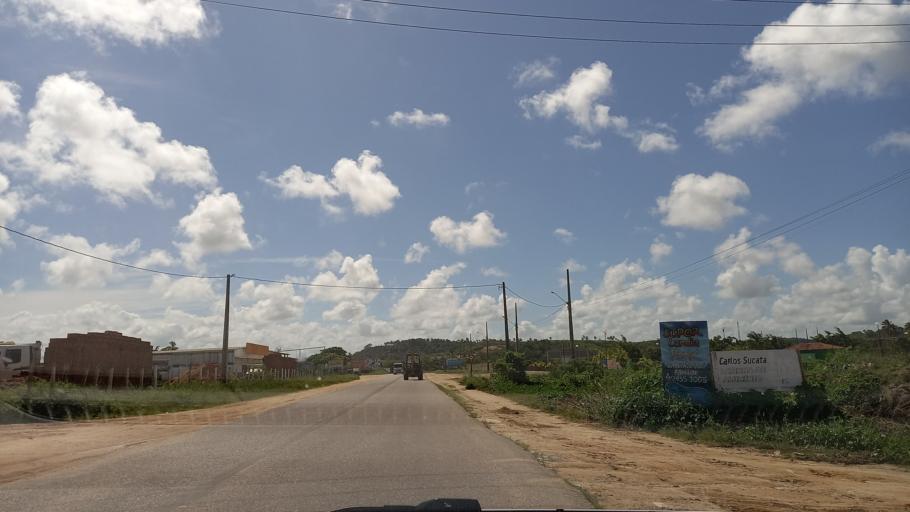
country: BR
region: Pernambuco
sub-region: Sao Jose Da Coroa Grande
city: Sao Jose da Coroa Grande
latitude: -8.8879
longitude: -35.1526
